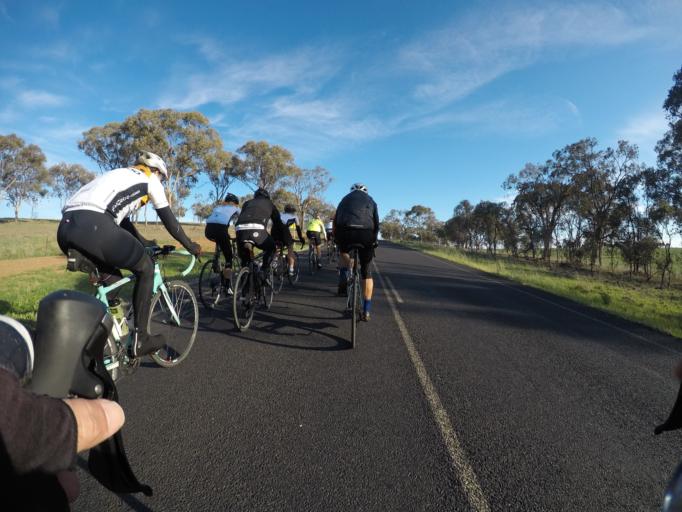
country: AU
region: New South Wales
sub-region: Cabonne
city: Molong
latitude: -32.9781
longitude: 148.7858
